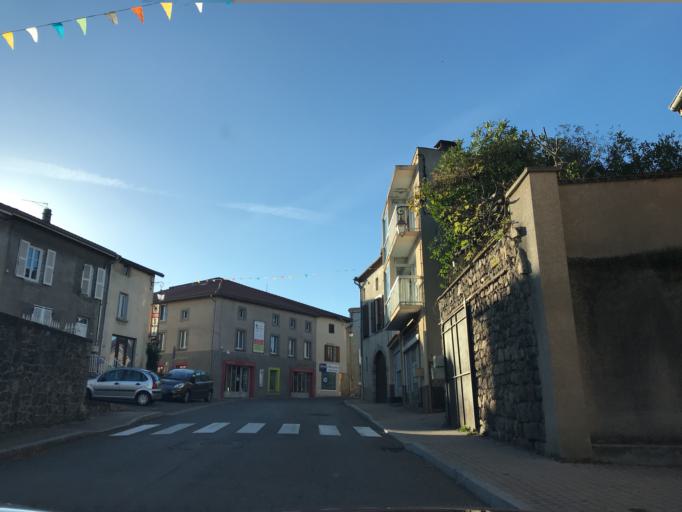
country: FR
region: Rhone-Alpes
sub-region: Departement de la Loire
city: Noiretable
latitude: 45.8166
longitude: 3.7668
